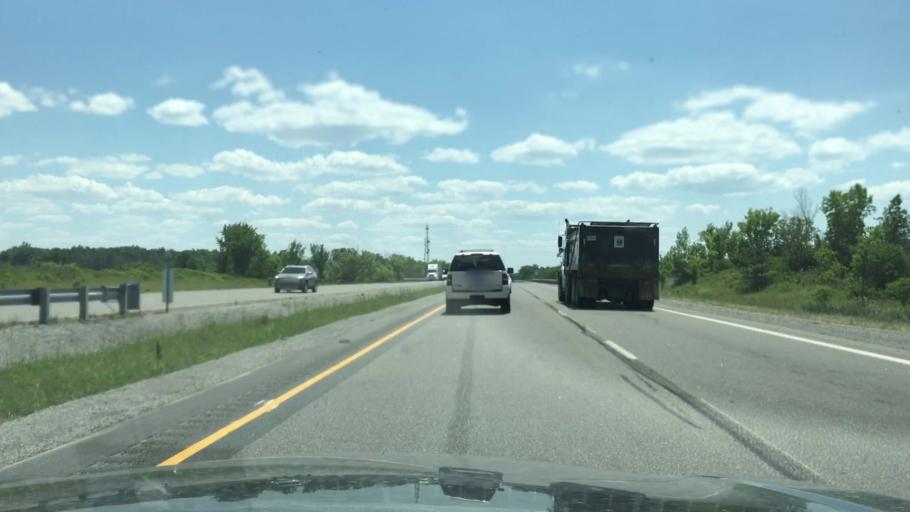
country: CA
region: Ontario
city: Niagara Falls
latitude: 43.0280
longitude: -79.1069
